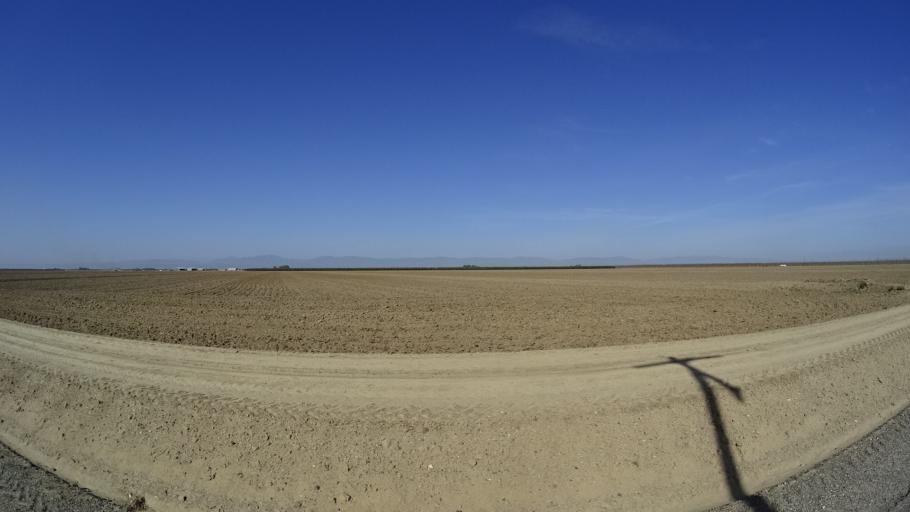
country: US
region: California
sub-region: Glenn County
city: Willows
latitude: 39.6076
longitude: -122.1169
